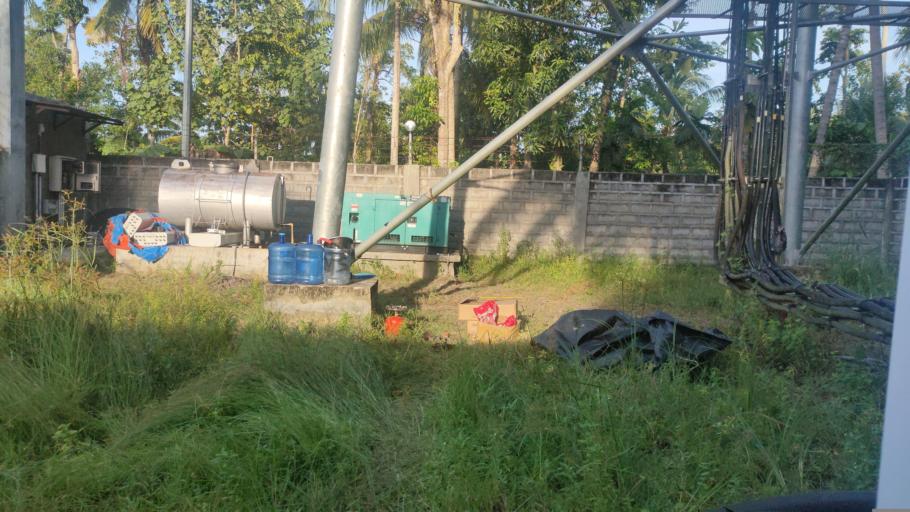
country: PH
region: Autonomous Region in Muslim Mindanao
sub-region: Province of Maguindanao
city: Pagatin
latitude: 6.9510
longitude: 124.4971
